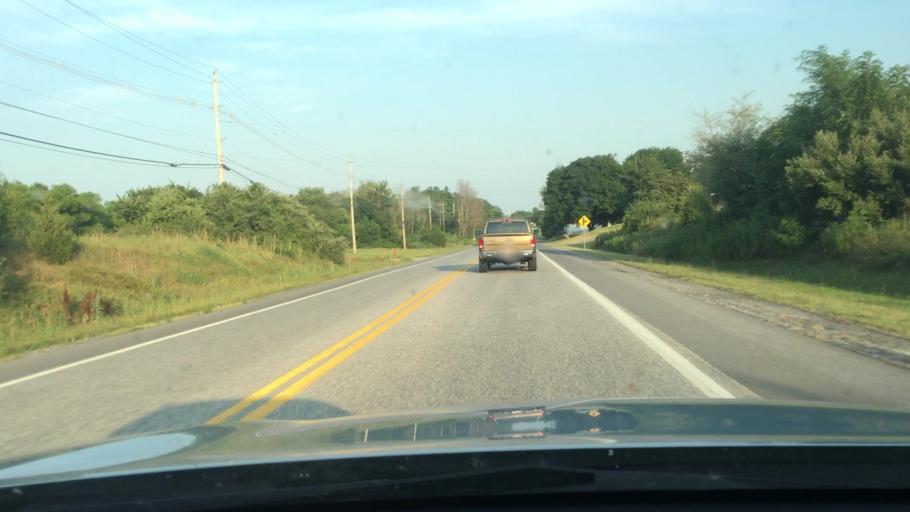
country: US
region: Pennsylvania
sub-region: York County
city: Dillsburg
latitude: 40.0898
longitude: -76.9501
